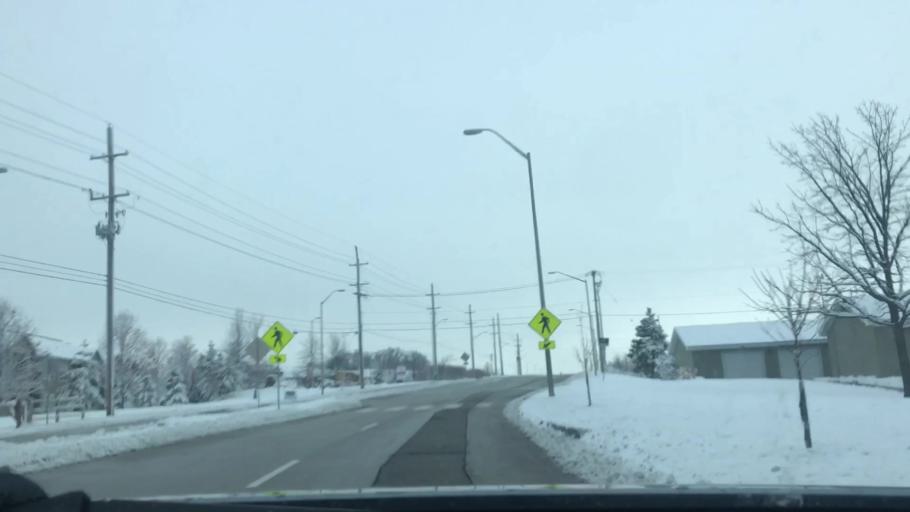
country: US
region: Missouri
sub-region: Platte County
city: Weatherby Lake
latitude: 39.2566
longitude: -94.6680
